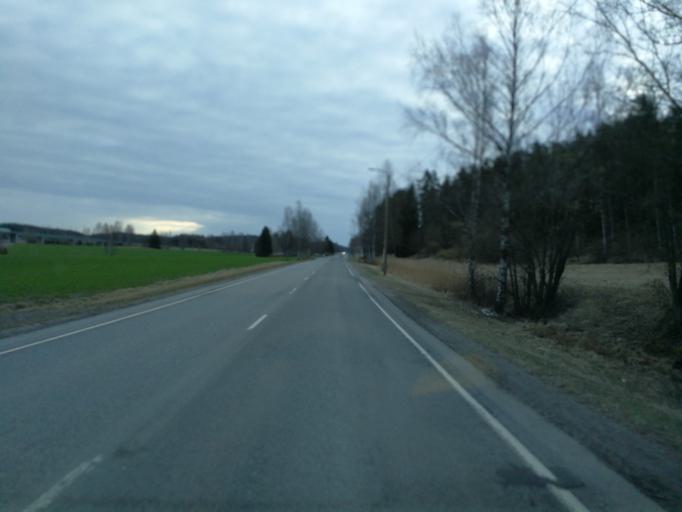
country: FI
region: Varsinais-Suomi
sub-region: Turku
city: Piikkioe
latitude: 60.4258
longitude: 22.5354
